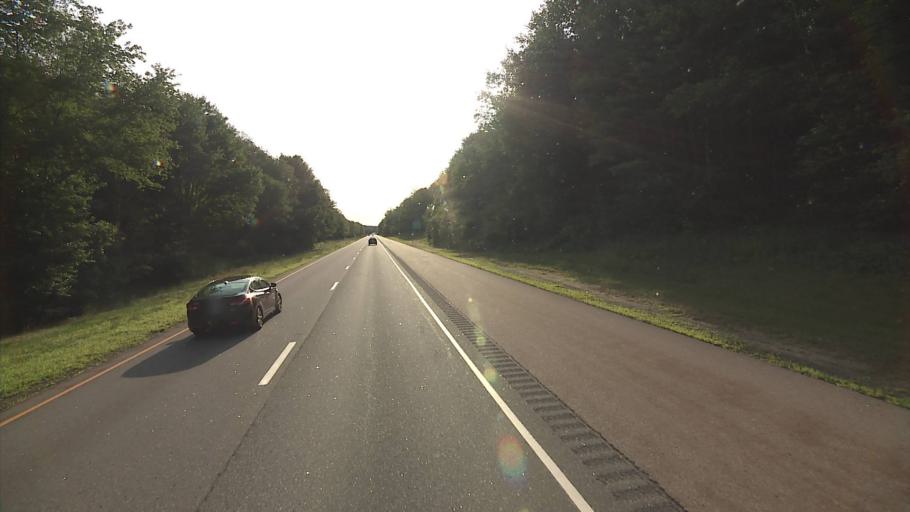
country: US
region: Connecticut
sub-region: New London County
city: Colchester
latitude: 41.5677
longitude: -72.2238
